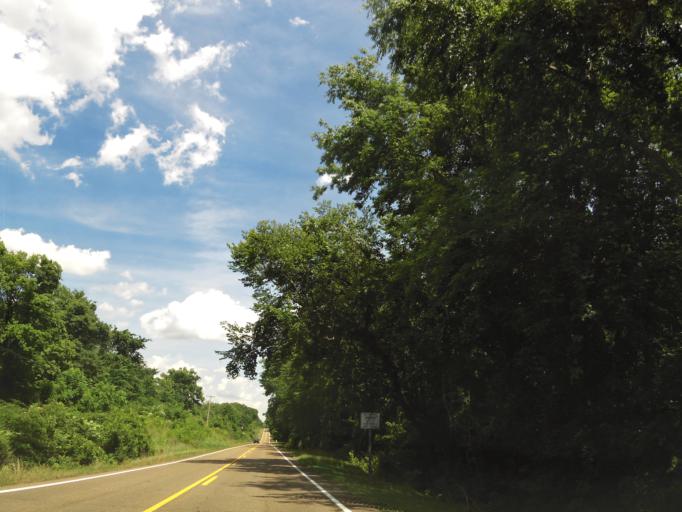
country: US
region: Tennessee
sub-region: Dyer County
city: Dyersburg
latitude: 36.0261
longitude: -89.3173
